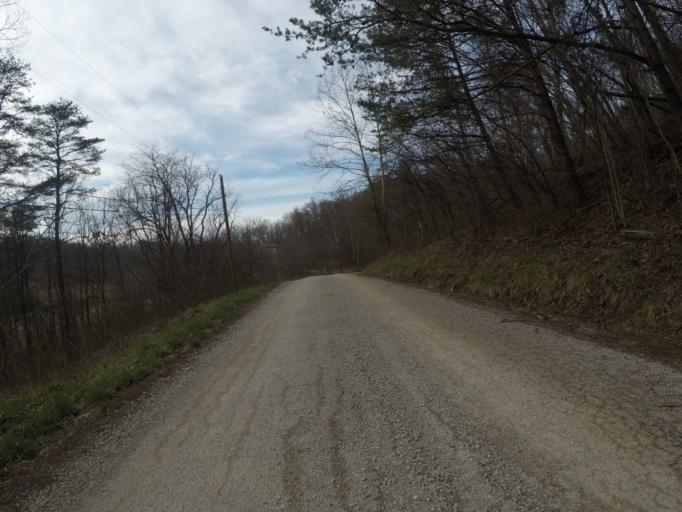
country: US
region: Ohio
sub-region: Lawrence County
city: Burlington
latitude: 38.4609
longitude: -82.5334
